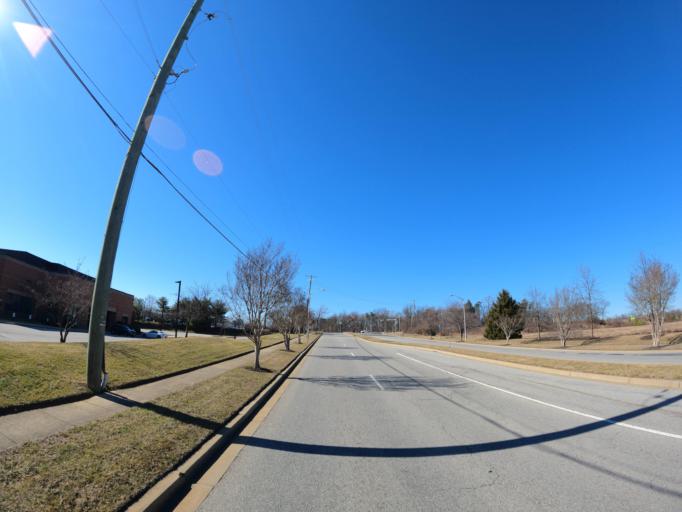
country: US
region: Maryland
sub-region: Prince George's County
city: Beltsville
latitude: 39.0635
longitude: -76.8892
